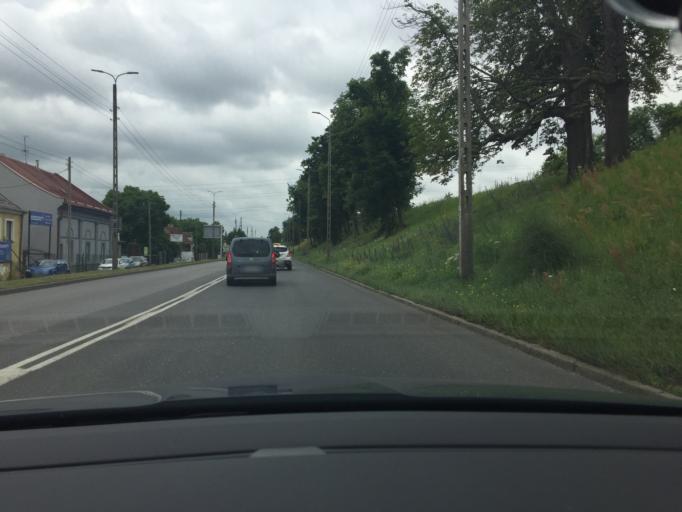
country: PL
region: Pomeranian Voivodeship
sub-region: Powiat gdanski
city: Pruszcz Gdanski
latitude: 54.2961
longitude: 18.6337
